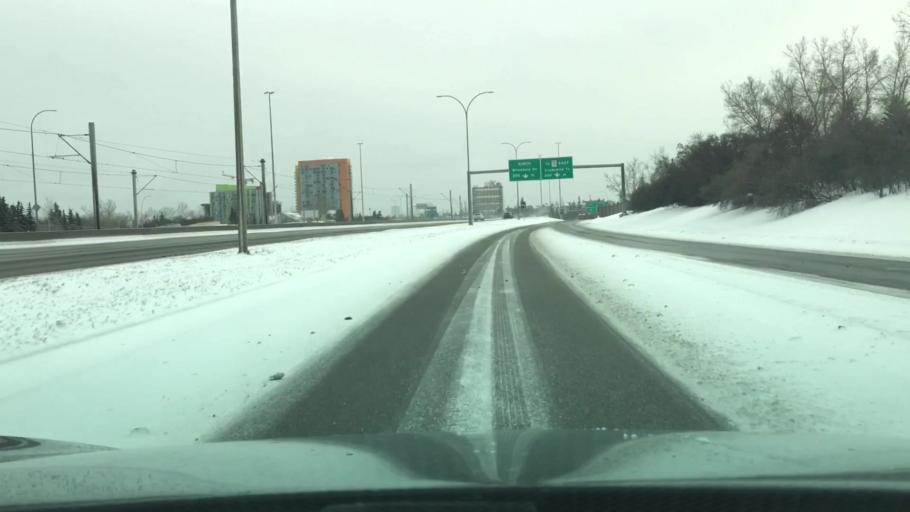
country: CA
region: Alberta
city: Calgary
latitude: 51.0911
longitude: -114.1385
